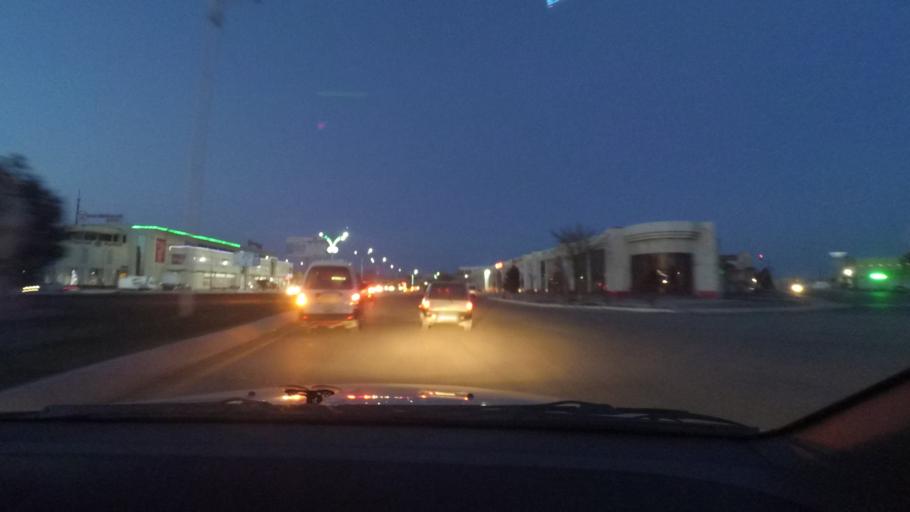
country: UZ
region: Bukhara
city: Bukhara
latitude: 39.7818
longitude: 64.4121
